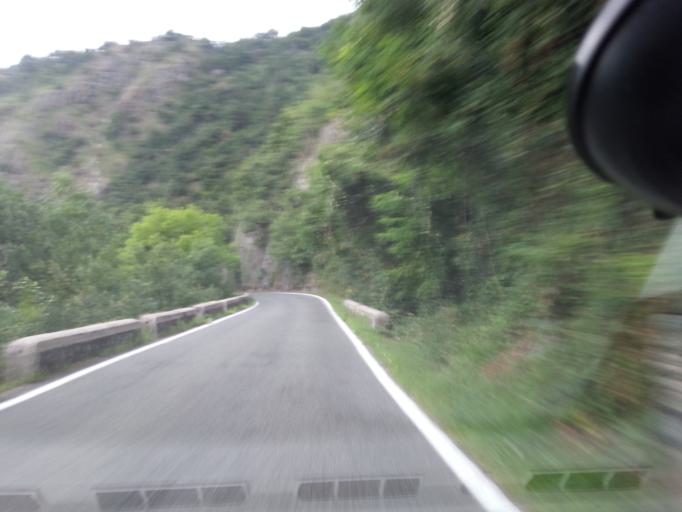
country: IT
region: Piedmont
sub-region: Provincia di Torino
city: Sant'Ambrogio di Torino
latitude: 45.0895
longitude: 7.3554
